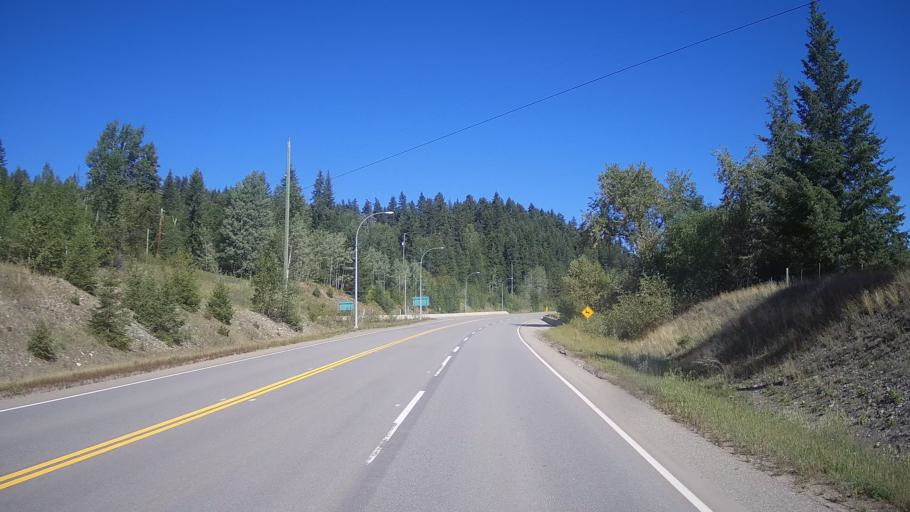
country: CA
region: British Columbia
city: Kamloops
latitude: 51.4560
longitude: -120.2265
